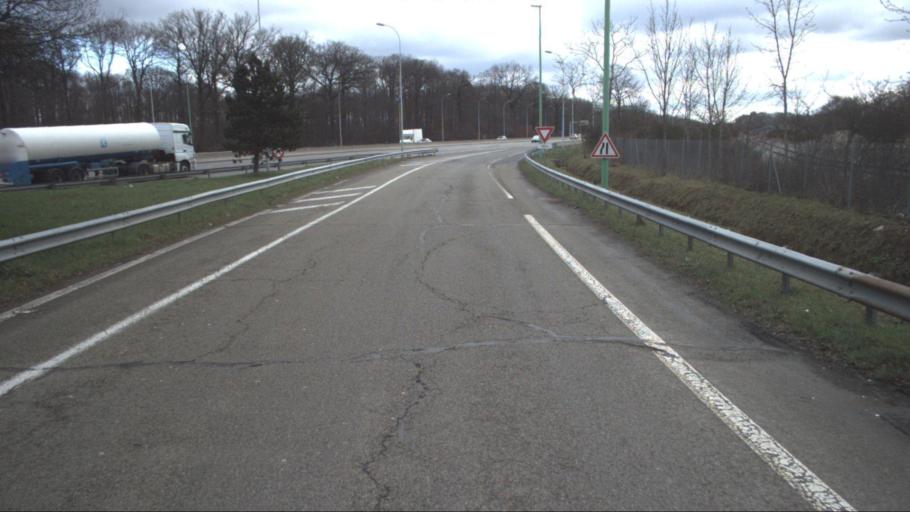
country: FR
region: Ile-de-France
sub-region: Departement des Yvelines
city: Saint-Cyr-l'Ecole
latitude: 48.7930
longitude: 2.0797
